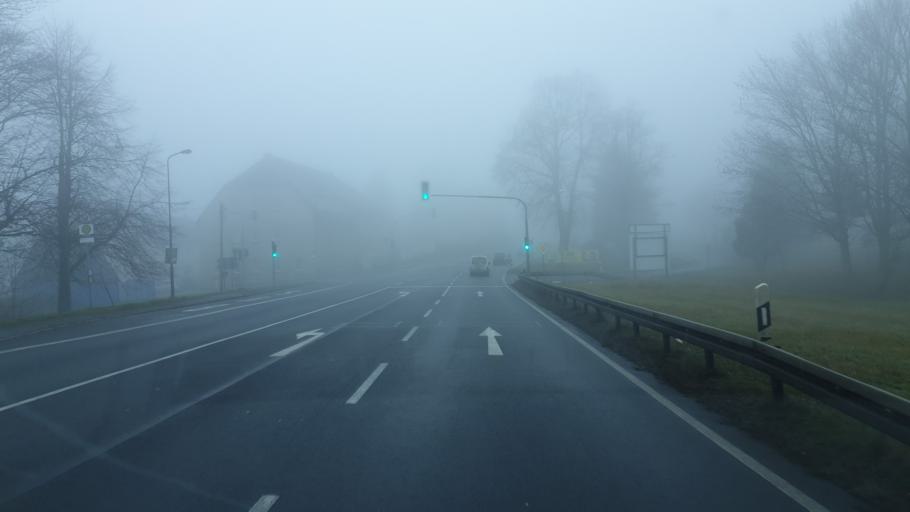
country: DE
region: Saxony
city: Grossolbersdorf
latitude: 50.7041
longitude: 13.1058
